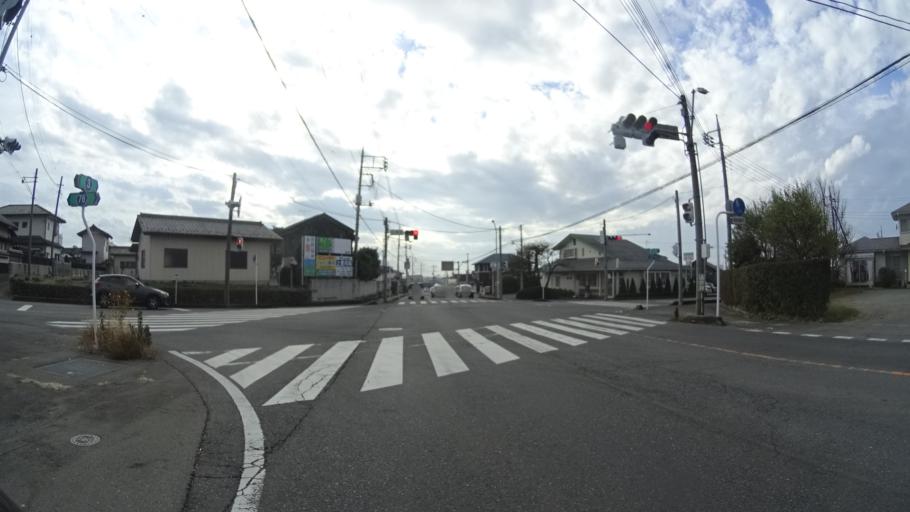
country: JP
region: Gunma
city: Maebashi-shi
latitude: 36.3979
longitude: 139.1173
